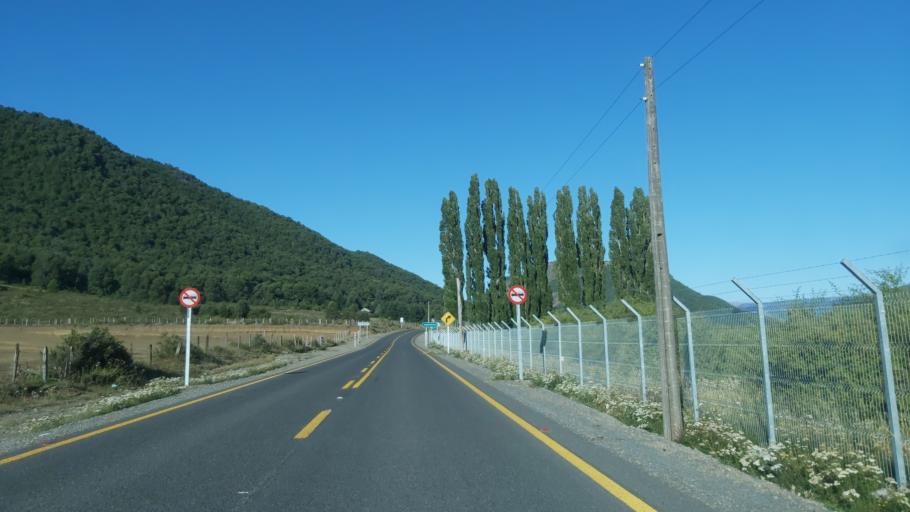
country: AR
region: Neuquen
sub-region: Departamento de Loncopue
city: Loncopue
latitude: -38.4473
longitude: -71.3607
